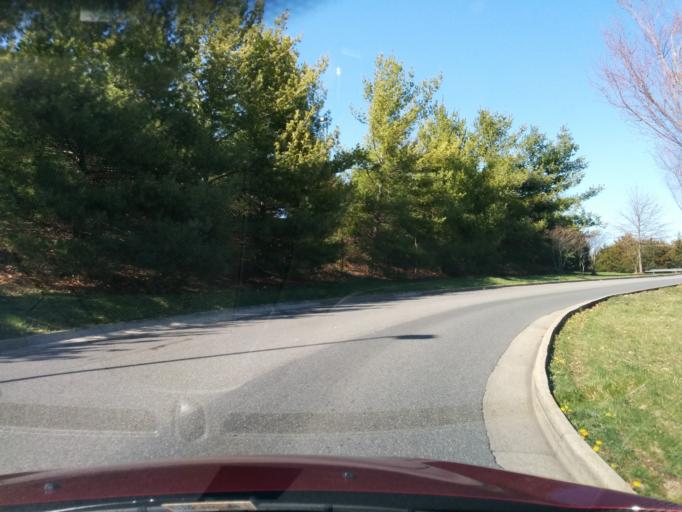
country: US
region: Virginia
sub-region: Rockbridge County
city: East Lexington
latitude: 37.8047
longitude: -79.4081
